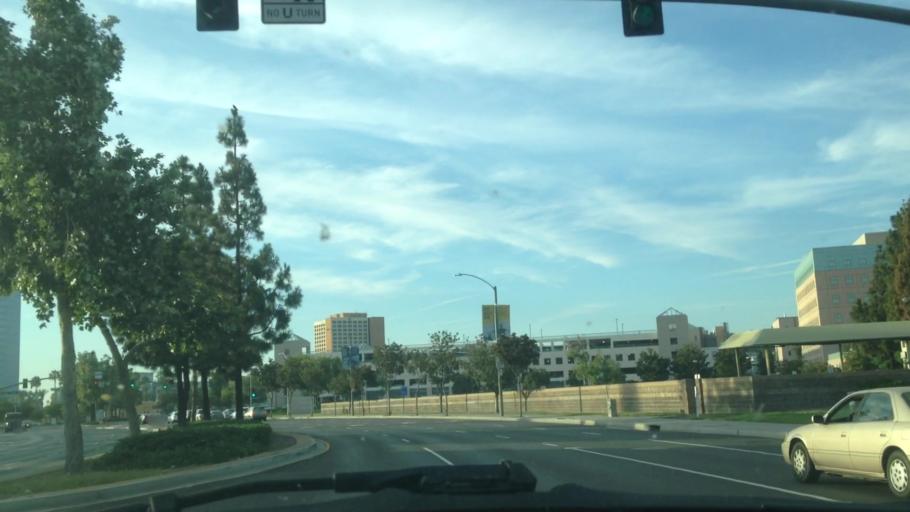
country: US
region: California
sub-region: Orange County
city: Orange
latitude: 33.7824
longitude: -117.8890
